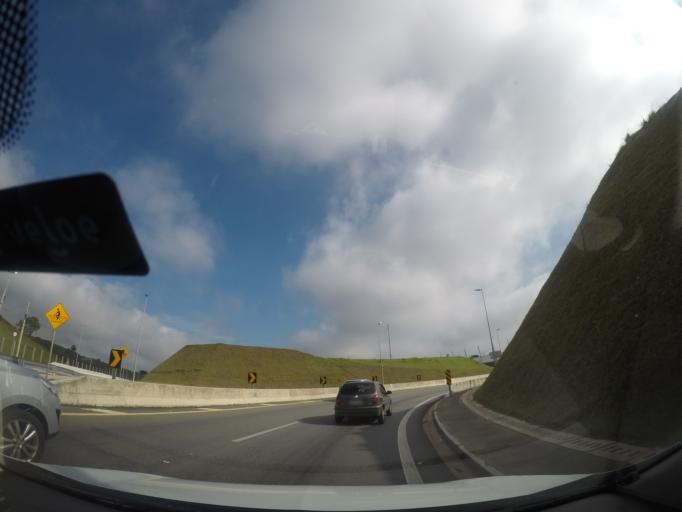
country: BR
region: Sao Paulo
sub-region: Jundiai
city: Jundiai
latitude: -23.2104
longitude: -46.8955
